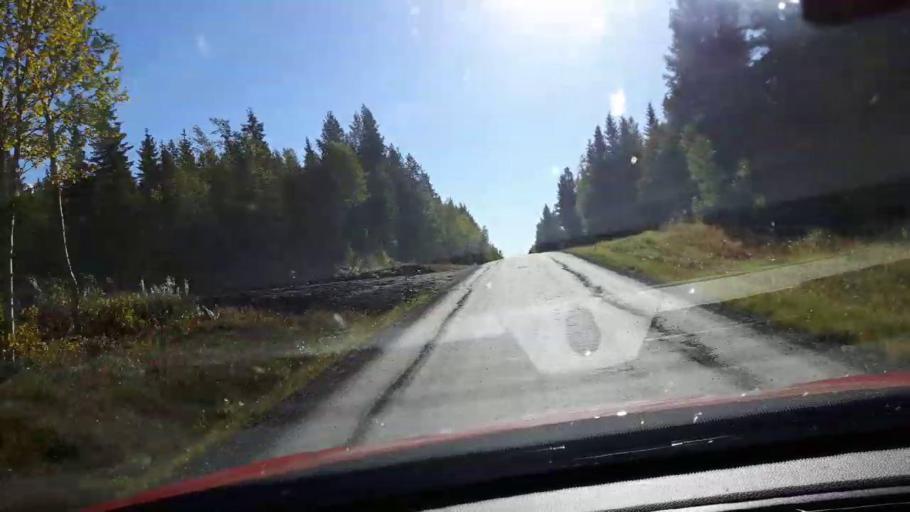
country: NO
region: Nord-Trondelag
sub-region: Lierne
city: Sandvika
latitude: 64.6067
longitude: 13.9617
